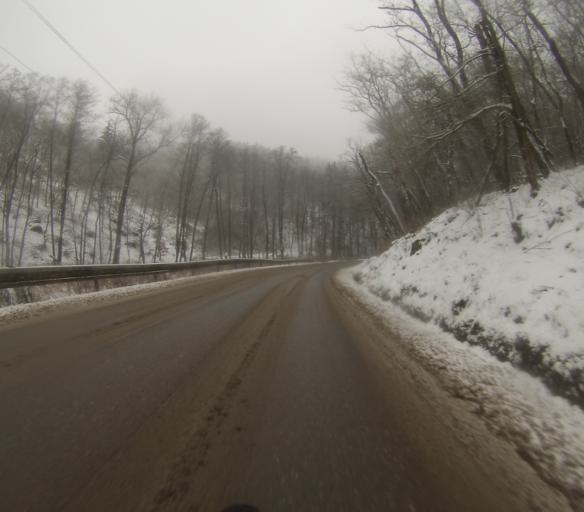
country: CZ
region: South Moravian
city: Orechov
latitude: 49.1356
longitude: 16.5275
